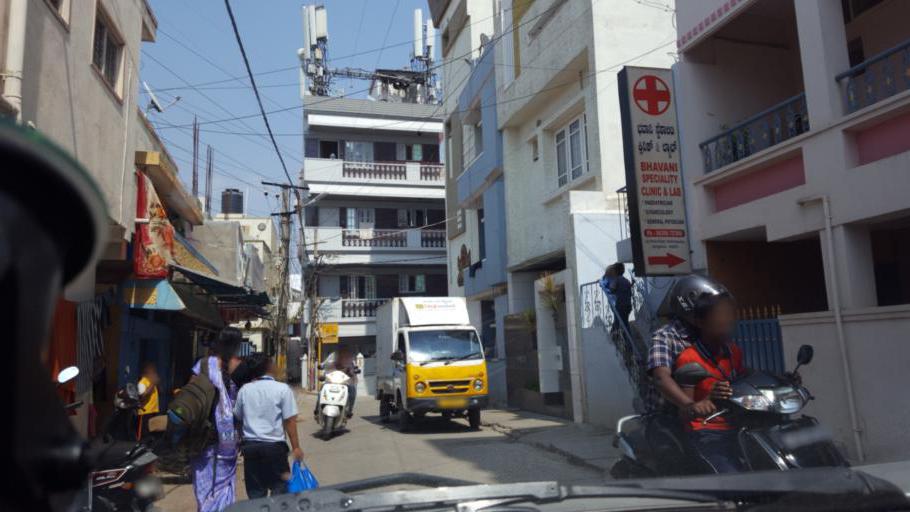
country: IN
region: Karnataka
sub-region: Bangalore Urban
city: Bangalore
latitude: 12.9760
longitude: 77.6706
